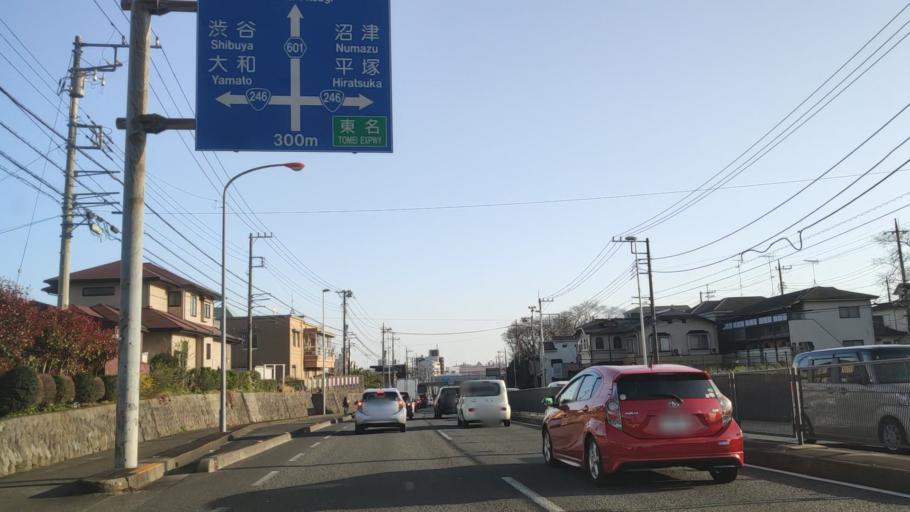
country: JP
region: Kanagawa
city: Zama
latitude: 35.4682
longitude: 139.3683
